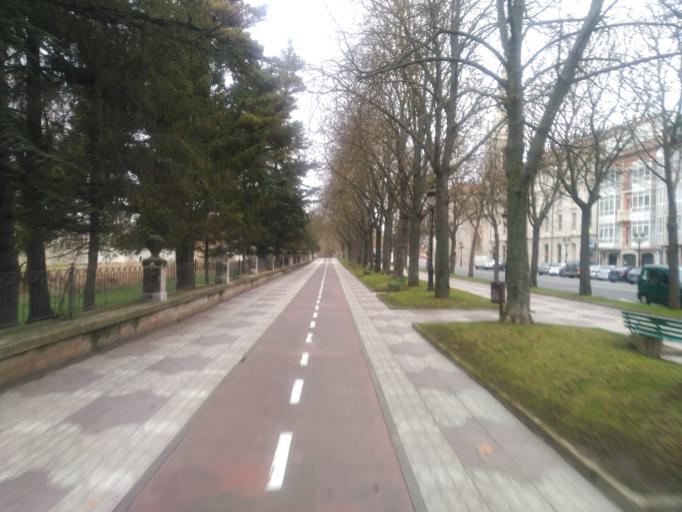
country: ES
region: Castille and Leon
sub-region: Provincia de Burgos
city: Burgos
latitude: 42.3380
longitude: -3.7052
